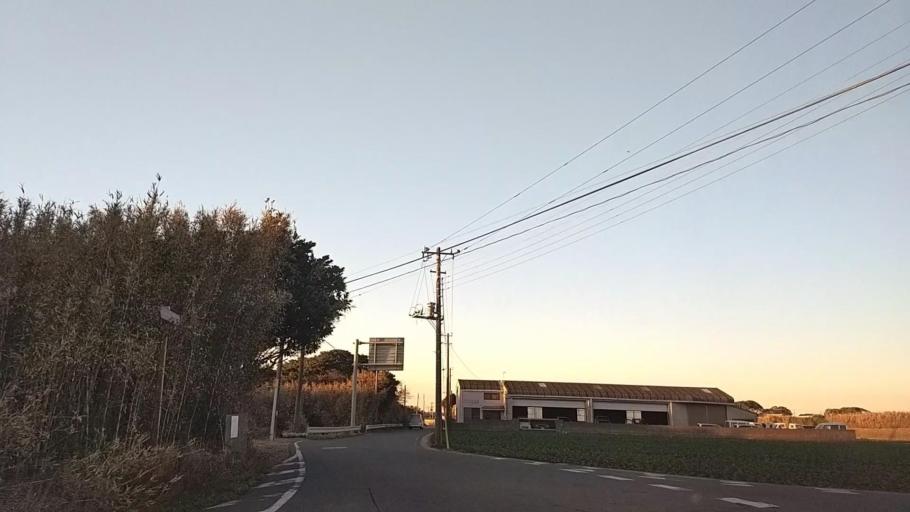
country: JP
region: Chiba
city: Hasaki
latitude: 35.7061
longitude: 140.8469
